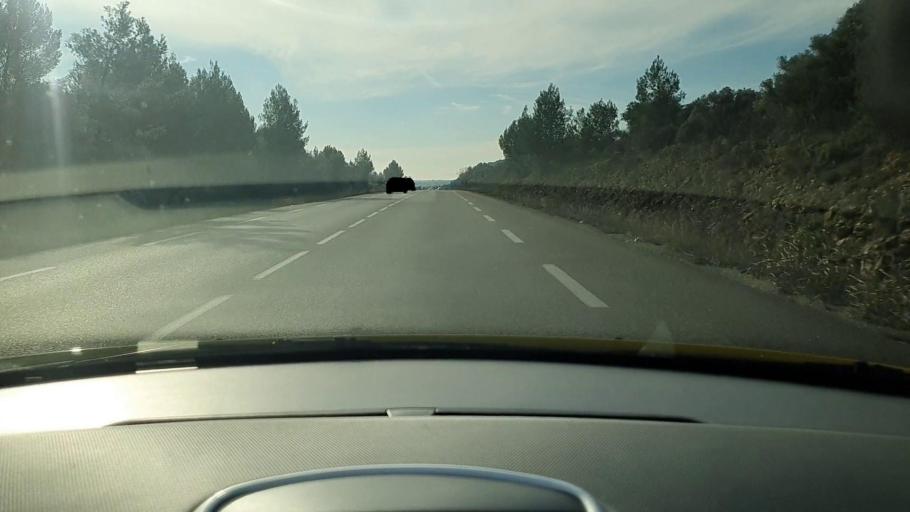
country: FR
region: Languedoc-Roussillon
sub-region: Departement du Gard
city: Comps
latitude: 43.8238
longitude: 4.6133
